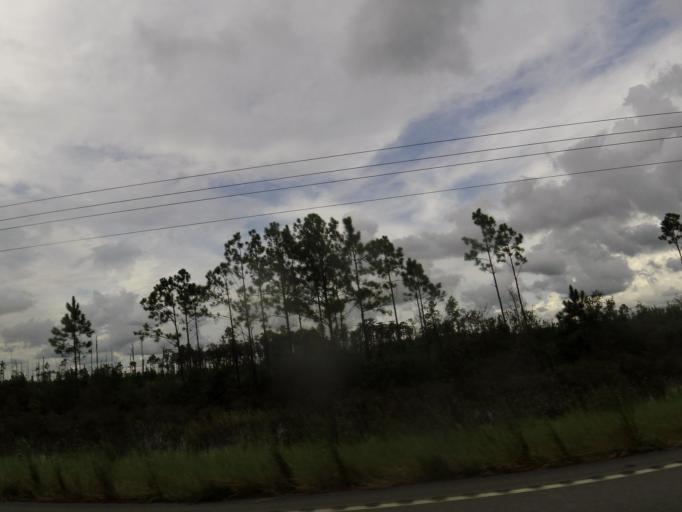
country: US
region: Florida
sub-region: Baker County
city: Macclenny
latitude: 30.5244
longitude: -82.1798
